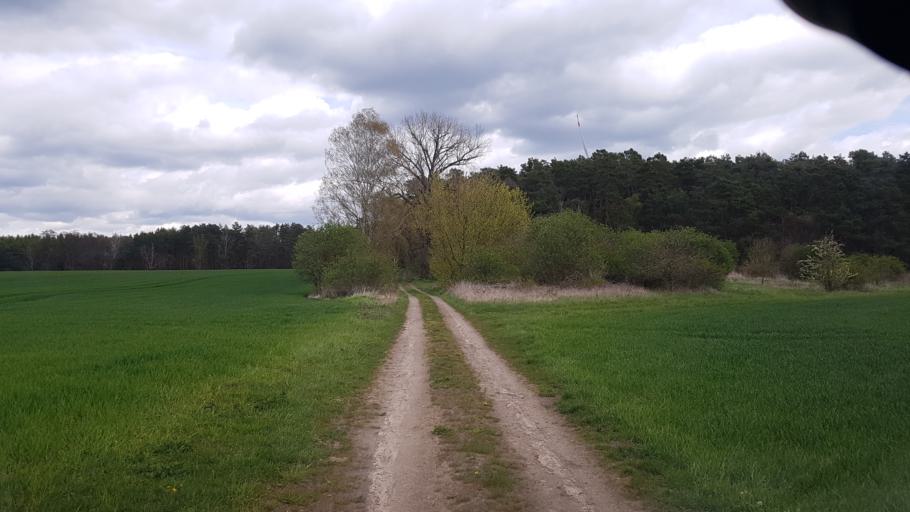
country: DE
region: Brandenburg
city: Finsterwalde
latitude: 51.6306
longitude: 13.7765
